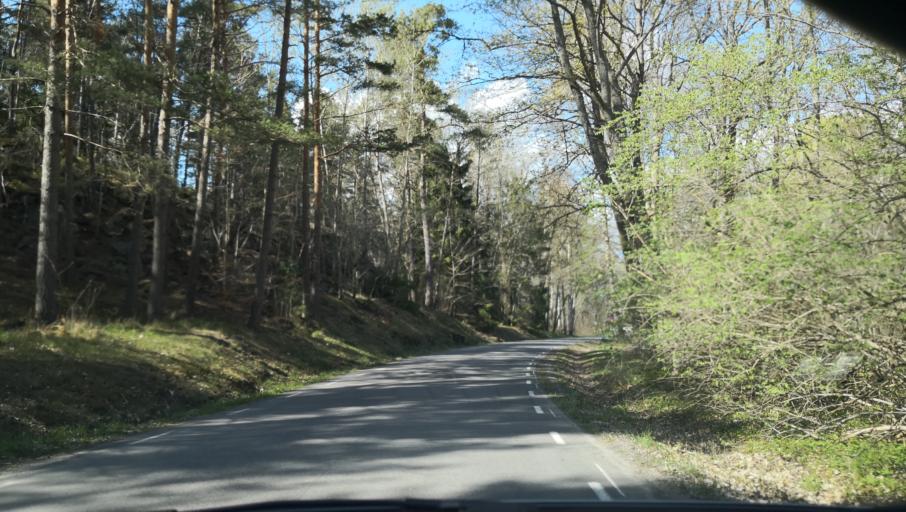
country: SE
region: Stockholm
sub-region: Varmdo Kommun
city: Hemmesta
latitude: 59.4101
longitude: 18.4950
